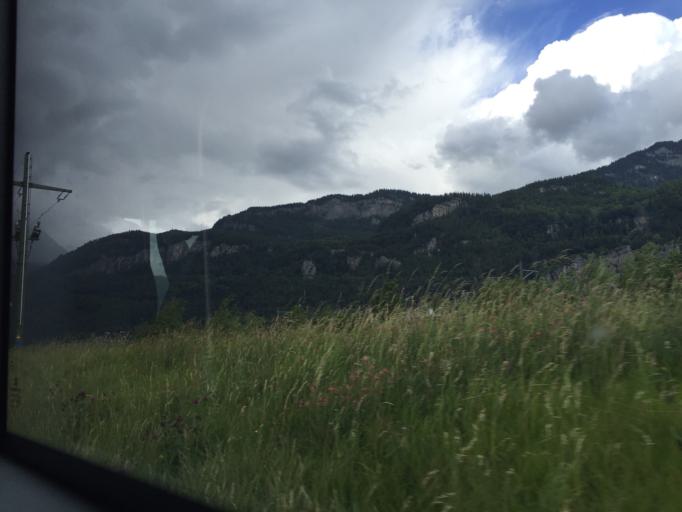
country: CH
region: Bern
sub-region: Interlaken-Oberhasli District
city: Meiringen
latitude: 46.7315
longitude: 8.1634
